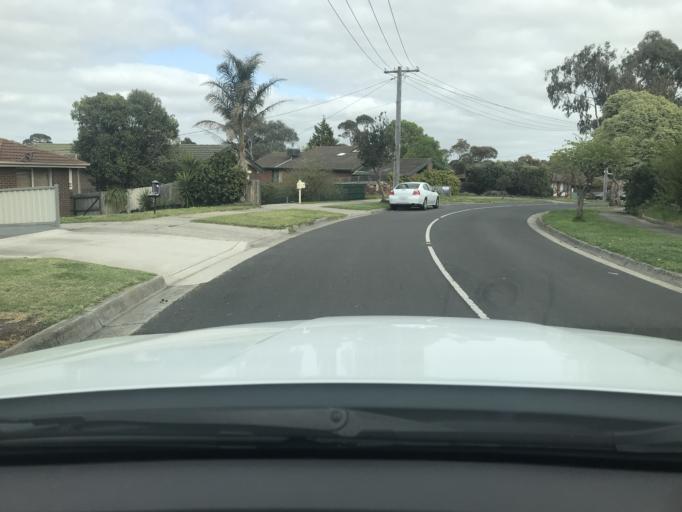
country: AU
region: Victoria
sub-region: Hume
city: Craigieburn
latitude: -37.6001
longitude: 144.9284
